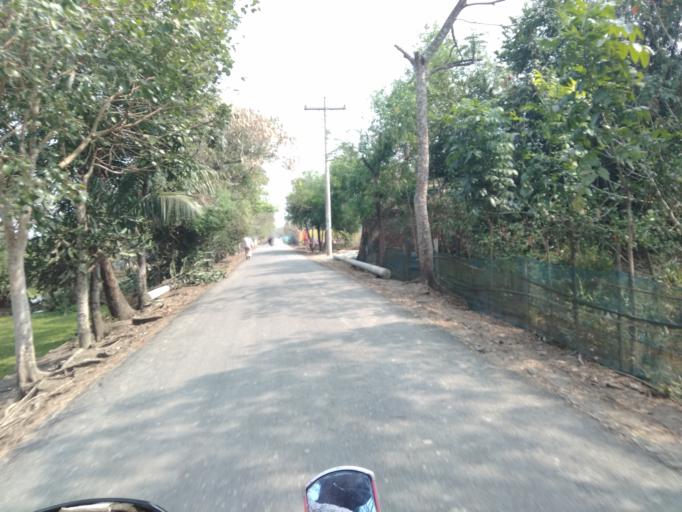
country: IN
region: West Bengal
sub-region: North 24 Parganas
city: Gosaba
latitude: 22.2310
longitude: 89.1568
